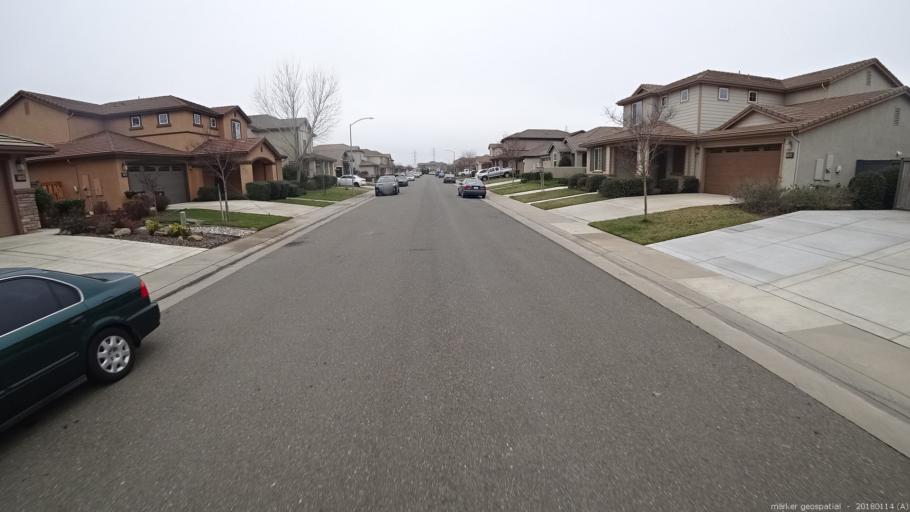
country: US
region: California
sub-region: Sacramento County
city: Gold River
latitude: 38.5348
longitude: -121.2261
